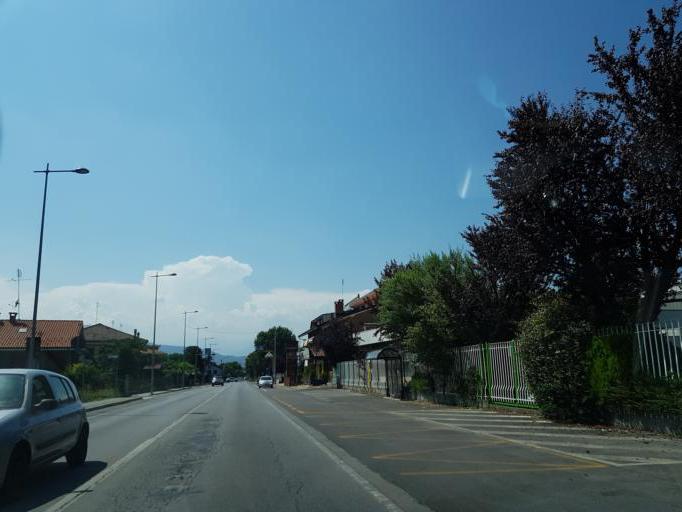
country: IT
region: Piedmont
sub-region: Provincia di Cuneo
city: San Defendente
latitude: 44.3956
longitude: 7.4923
